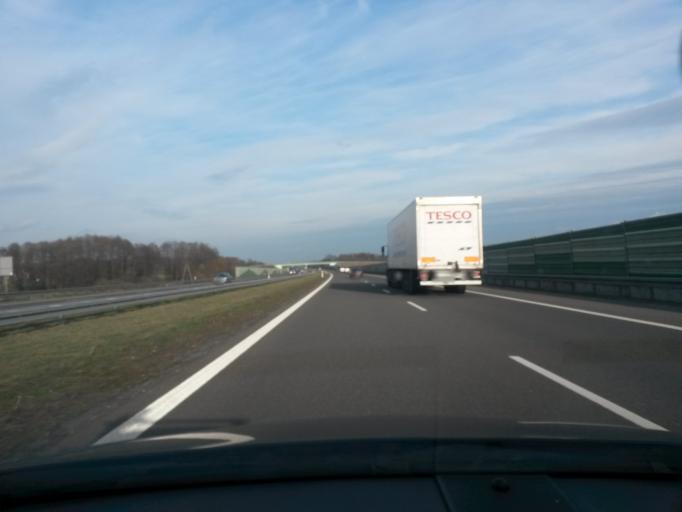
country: PL
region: Lodz Voivodeship
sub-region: Powiat zgierski
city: Zgierz
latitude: 51.8982
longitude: 19.4806
